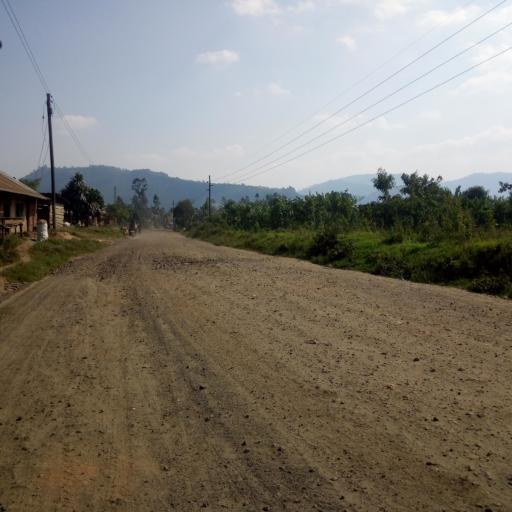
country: UG
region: Western Region
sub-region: Kisoro District
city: Kisoro
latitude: -1.2323
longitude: 29.7114
